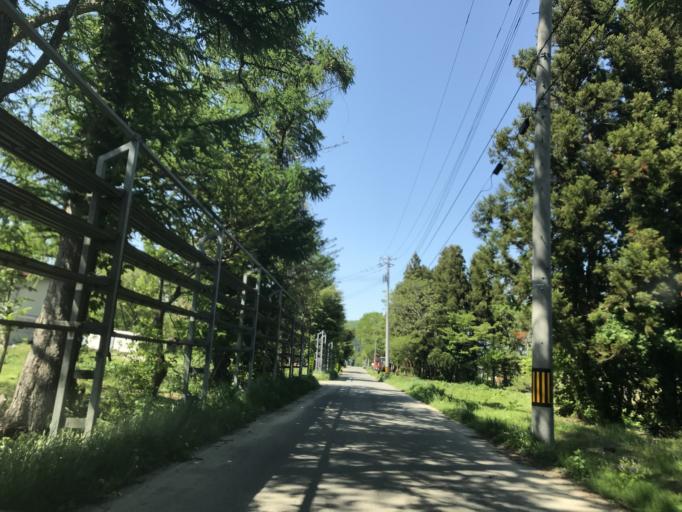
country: JP
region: Iwate
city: Shizukuishi
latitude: 39.5580
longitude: 140.8313
